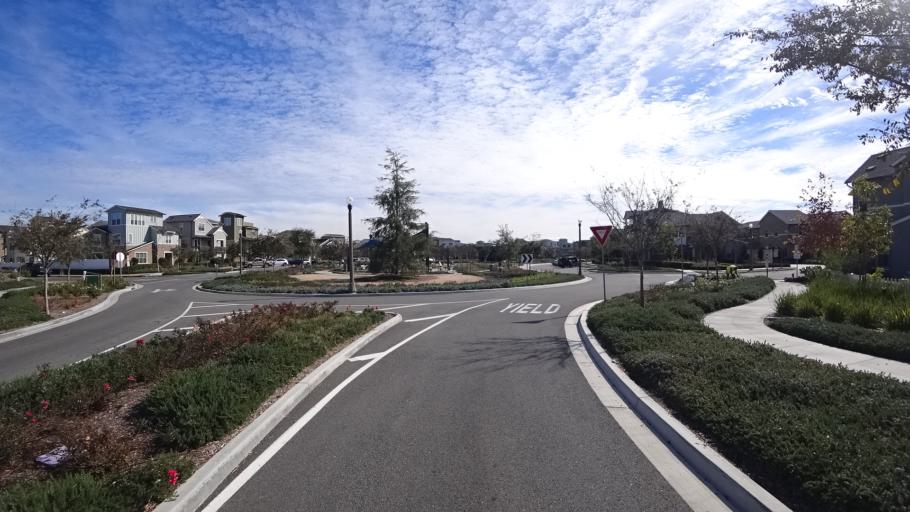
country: US
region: California
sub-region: Orange County
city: Ladera Ranch
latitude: 33.5446
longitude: -117.5994
